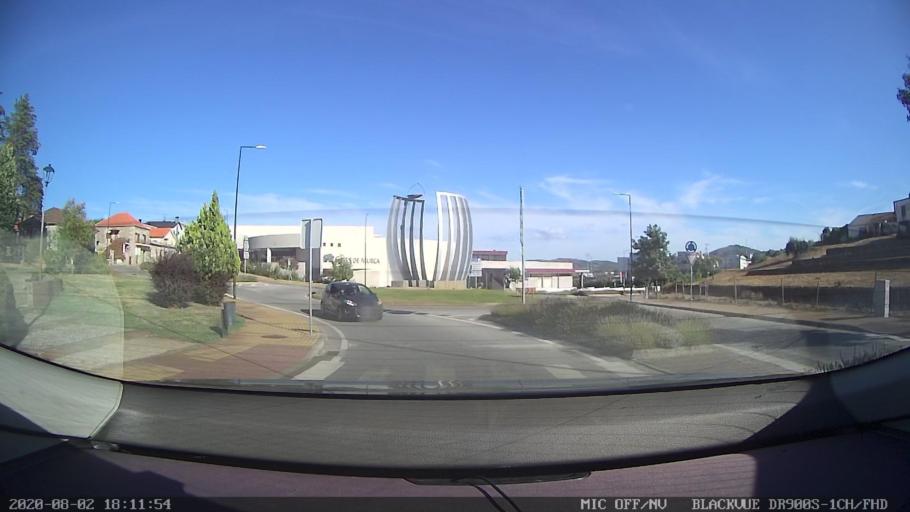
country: PT
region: Vila Real
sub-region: Murca
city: Murca
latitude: 41.4078
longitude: -7.4505
